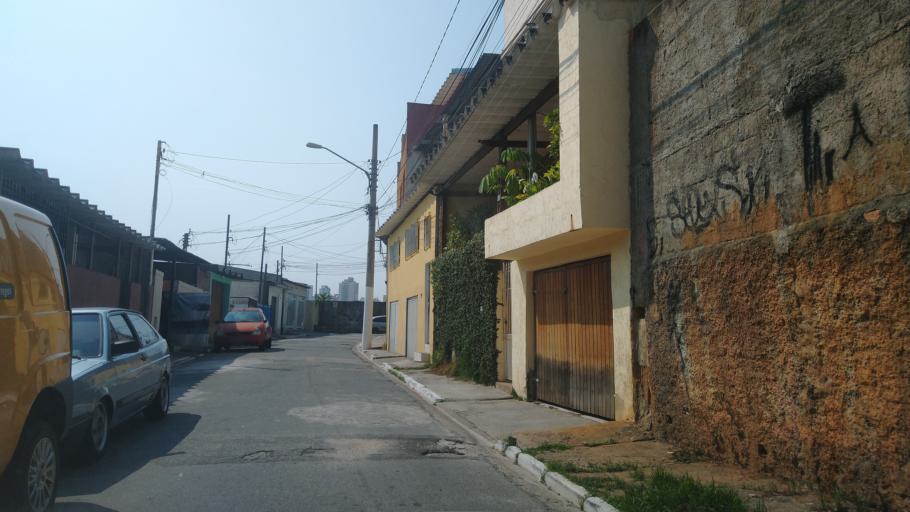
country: BR
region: Sao Paulo
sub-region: Sao Paulo
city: Sao Paulo
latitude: -23.4829
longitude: -46.6403
